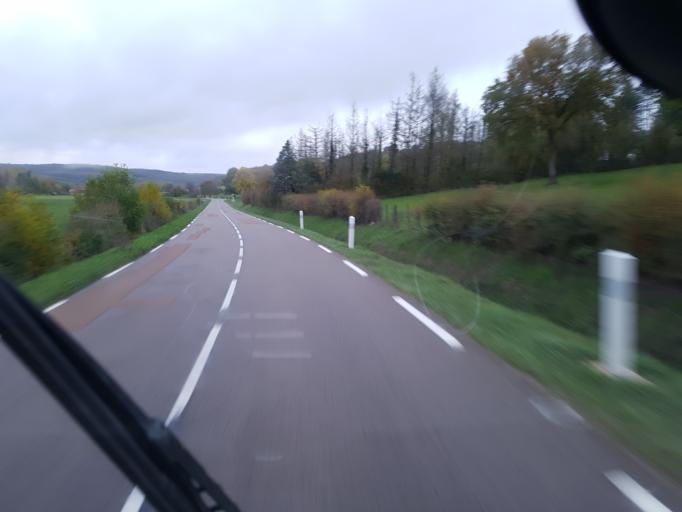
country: FR
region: Bourgogne
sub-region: Departement de la Cote-d'Or
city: Chatillon-sur-Seine
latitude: 47.6961
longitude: 4.6431
